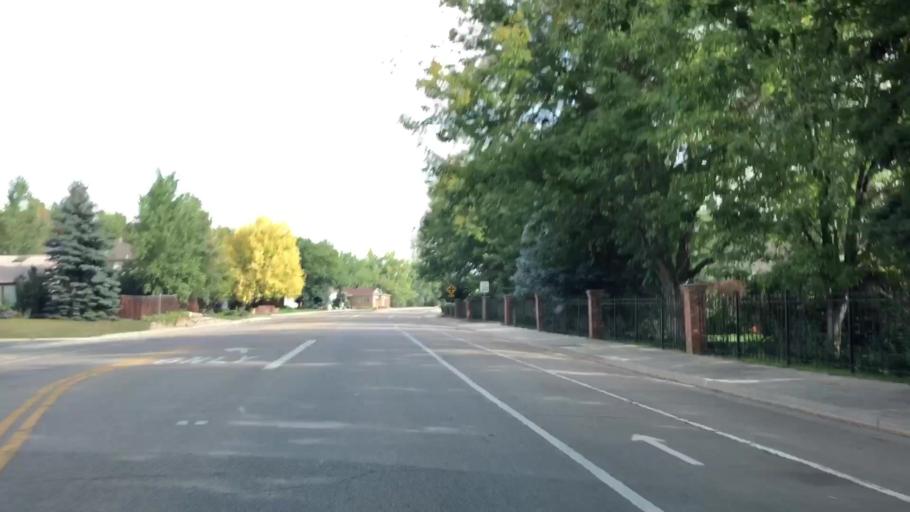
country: US
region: Colorado
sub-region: Larimer County
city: Loveland
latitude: 40.4175
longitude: -105.0535
